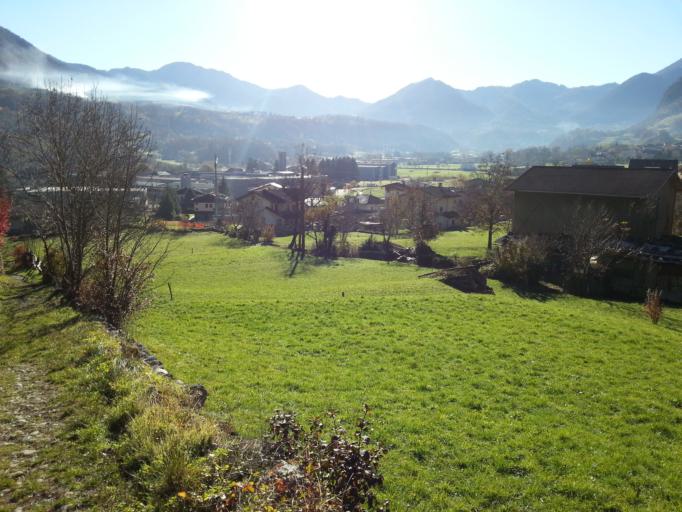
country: IT
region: Lombardy
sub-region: Provincia di Lecco
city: Pasturo
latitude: 45.9587
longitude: 9.4452
